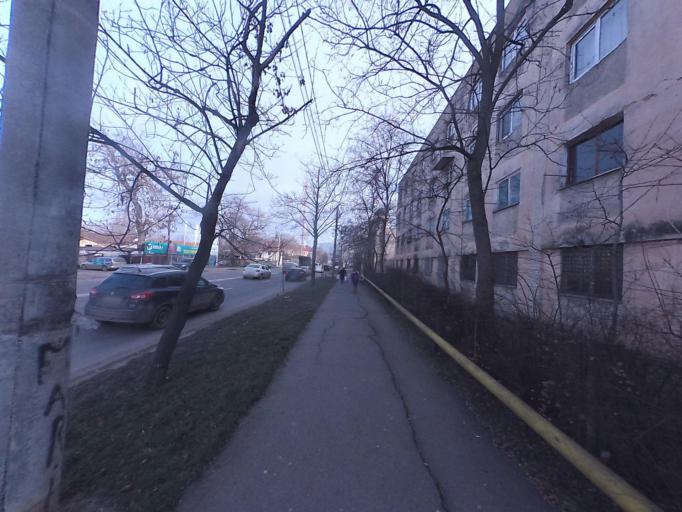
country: RO
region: Iasi
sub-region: Municipiul Iasi
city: Iasi
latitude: 47.1361
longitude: 27.5920
